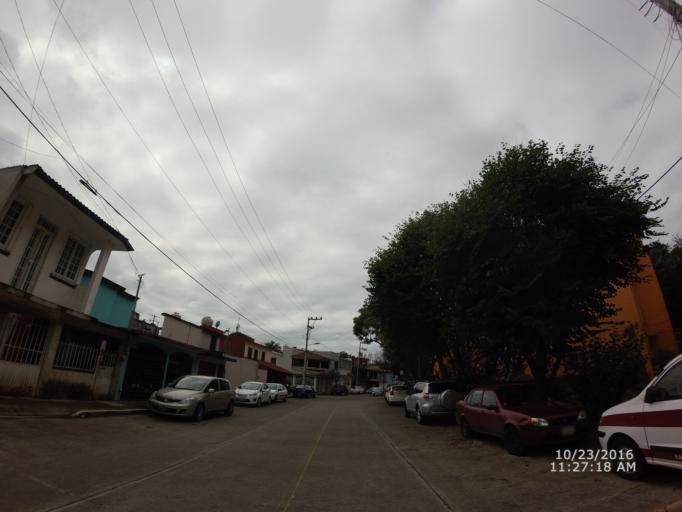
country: MX
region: Veracruz
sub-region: Tlalnelhuayocan
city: Guadalupe Victoria
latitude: 19.5483
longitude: -96.9402
